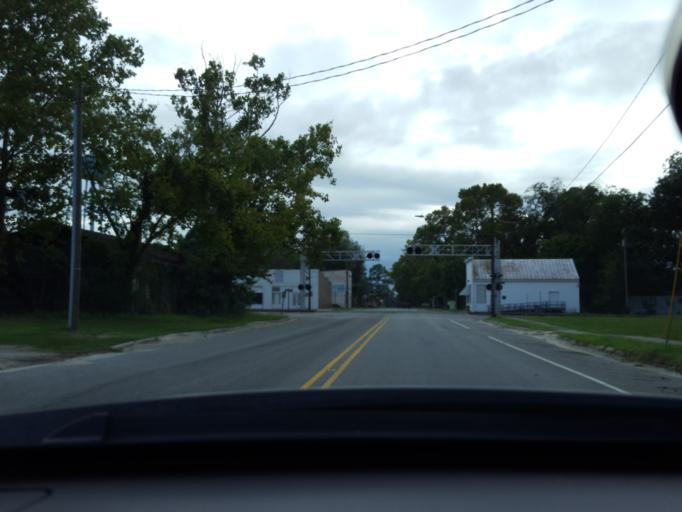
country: US
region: North Carolina
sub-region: Duplin County
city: Rose Hill
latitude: 34.8964
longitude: -78.0549
